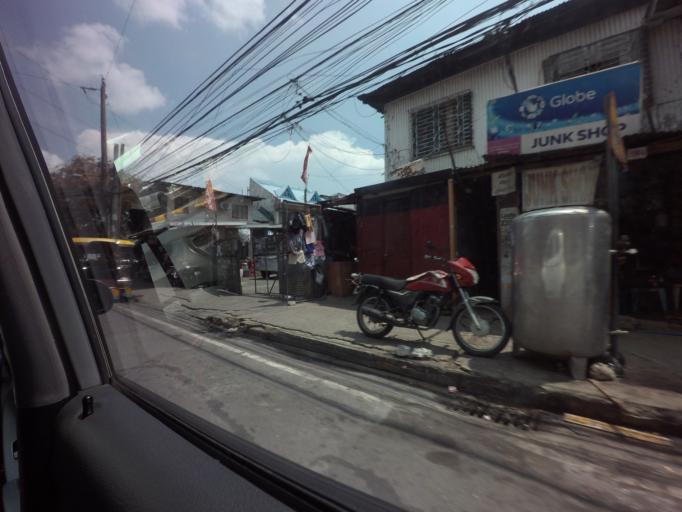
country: PH
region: Metro Manila
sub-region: City of Manila
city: Quiapo
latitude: 14.5888
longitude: 121.0065
